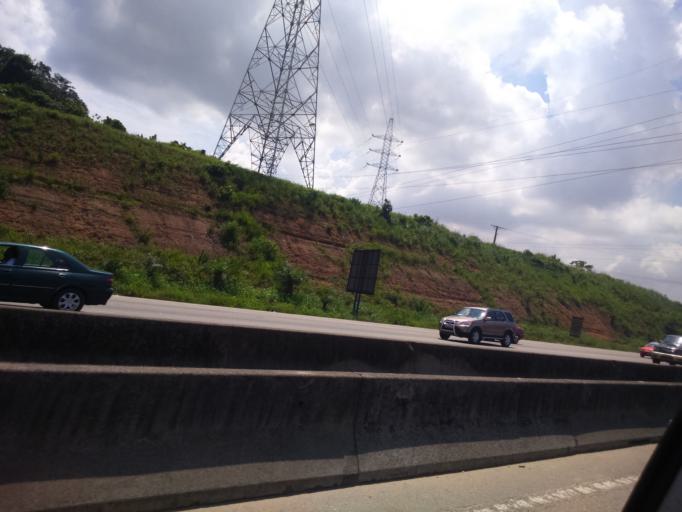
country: CI
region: Lagunes
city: Abobo
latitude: 5.3636
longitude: -4.0323
